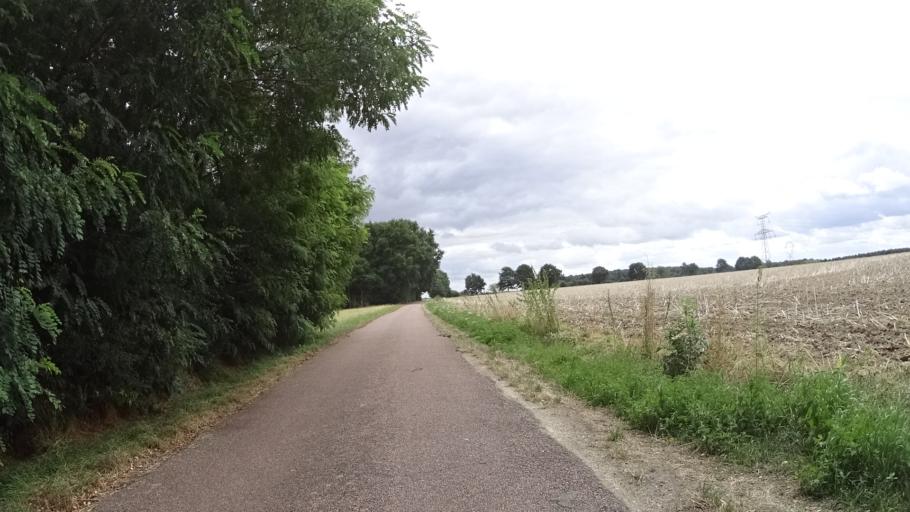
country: FR
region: Centre
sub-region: Departement du Loiret
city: Saint-Germain-des-Pres
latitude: 47.9440
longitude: 2.8181
